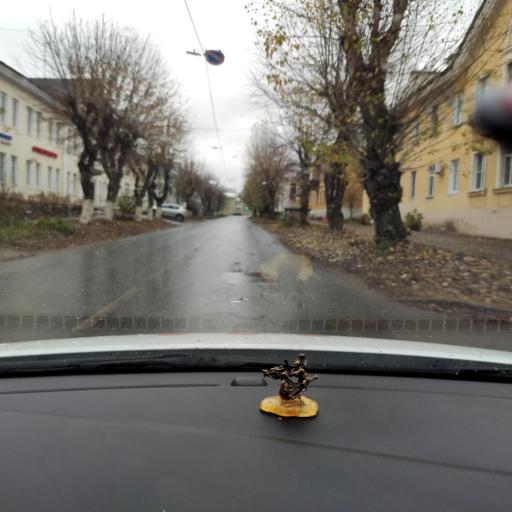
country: RU
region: Tatarstan
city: Vysokaya Gora
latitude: 55.8671
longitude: 49.2258
